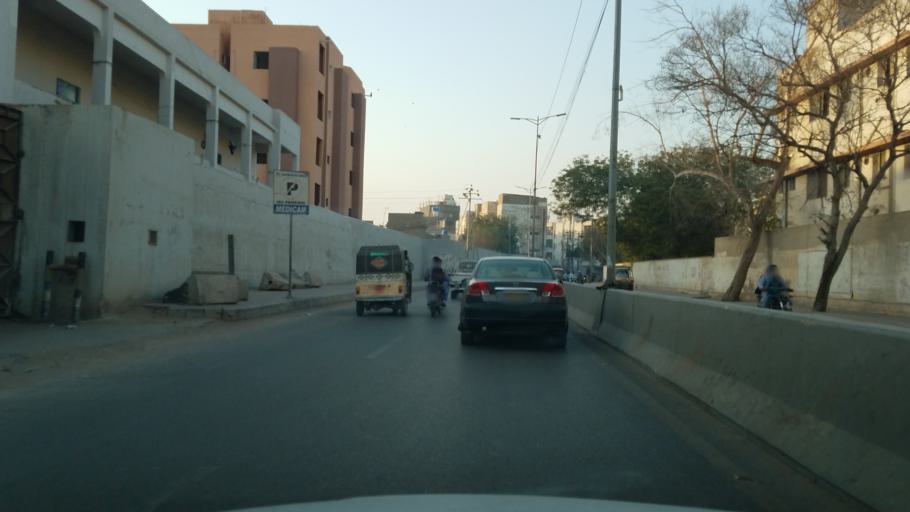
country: PK
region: Sindh
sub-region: Karachi District
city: Karachi
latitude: 24.8709
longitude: 67.0223
